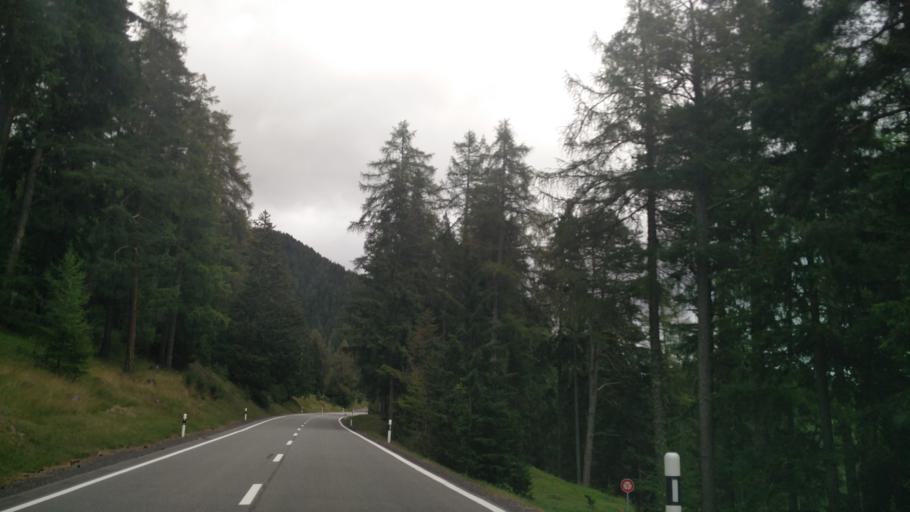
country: CH
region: Grisons
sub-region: Inn District
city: Zernez
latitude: 46.6924
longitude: 10.1288
